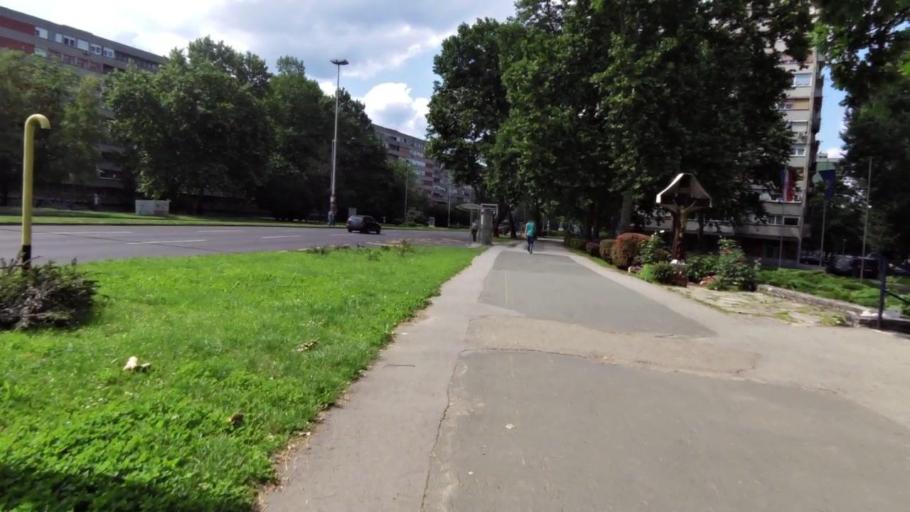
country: HR
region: Grad Zagreb
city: Novi Zagreb
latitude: 45.7885
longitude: 15.9456
